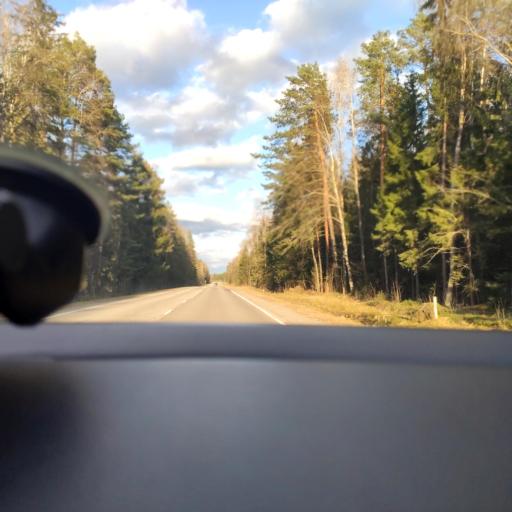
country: RU
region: Moskovskaya
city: Shaturtorf
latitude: 55.4300
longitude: 39.3735
